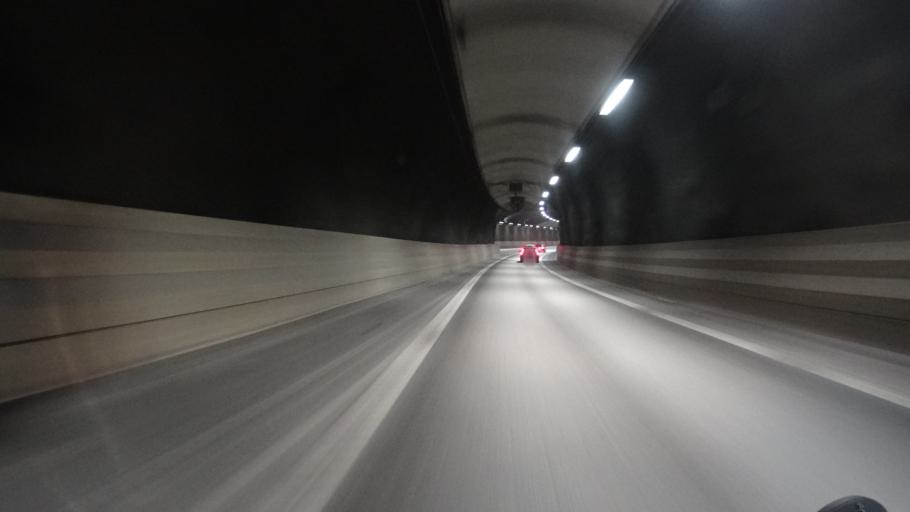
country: SE
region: Stockholm
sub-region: Stockholms Kommun
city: Arsta
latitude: 59.2911
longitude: 18.0868
